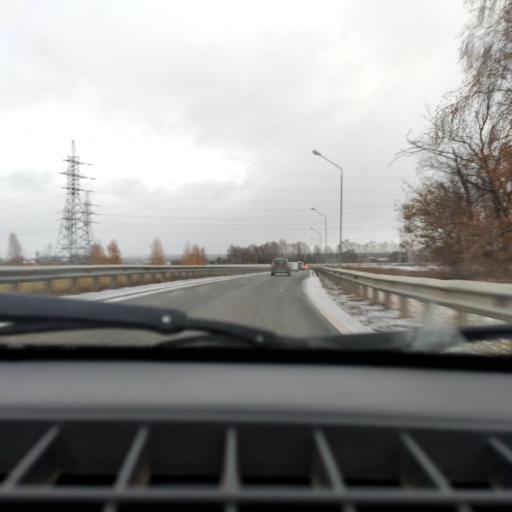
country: RU
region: Bashkortostan
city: Avdon
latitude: 54.6756
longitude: 55.7973
